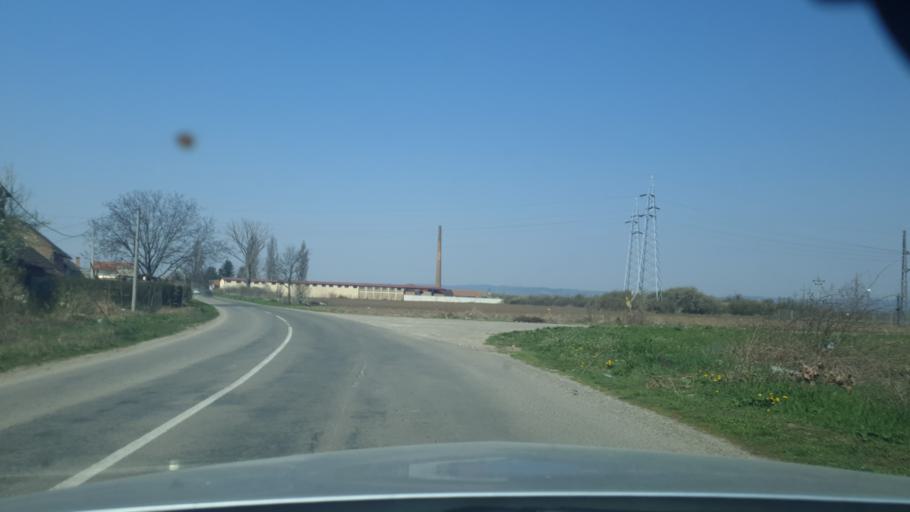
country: RS
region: Autonomna Pokrajina Vojvodina
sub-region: Sremski Okrug
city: Ruma
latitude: 45.0082
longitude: 19.7873
